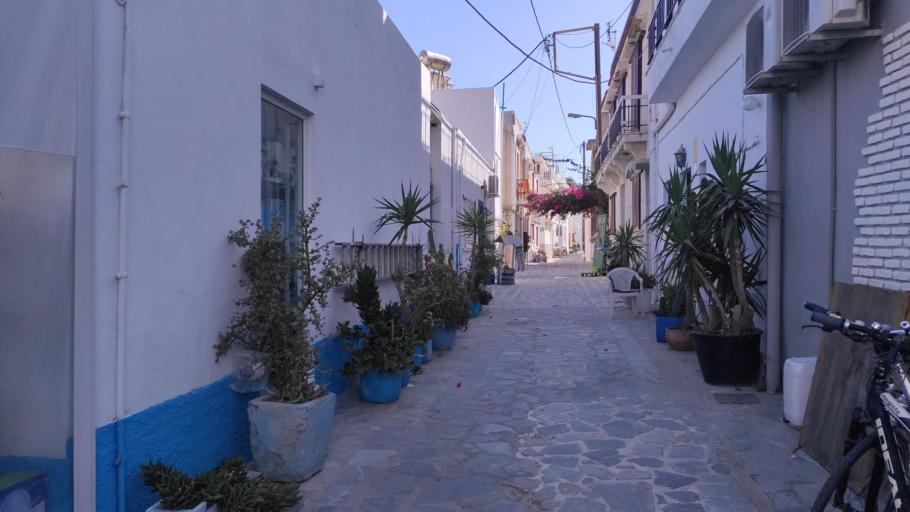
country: GR
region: South Aegean
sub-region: Nomos Dodekanisou
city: Kardamaina
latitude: 36.7827
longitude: 27.1431
